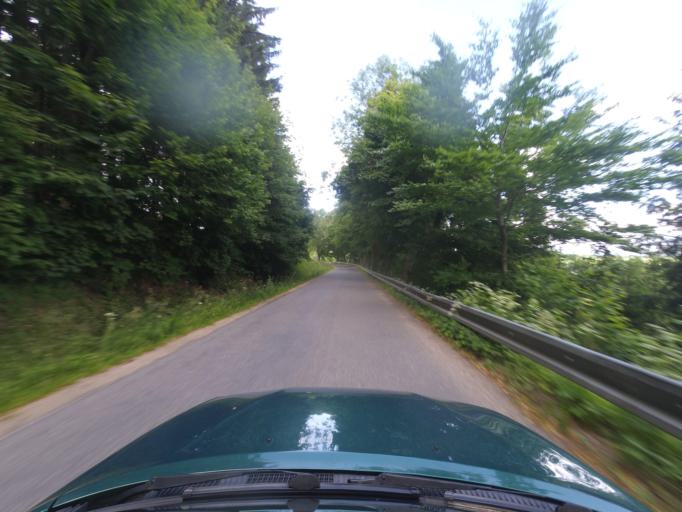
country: PL
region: Lower Silesian Voivodeship
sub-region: Powiat klodzki
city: Miedzylesie
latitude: 50.1205
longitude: 16.5904
